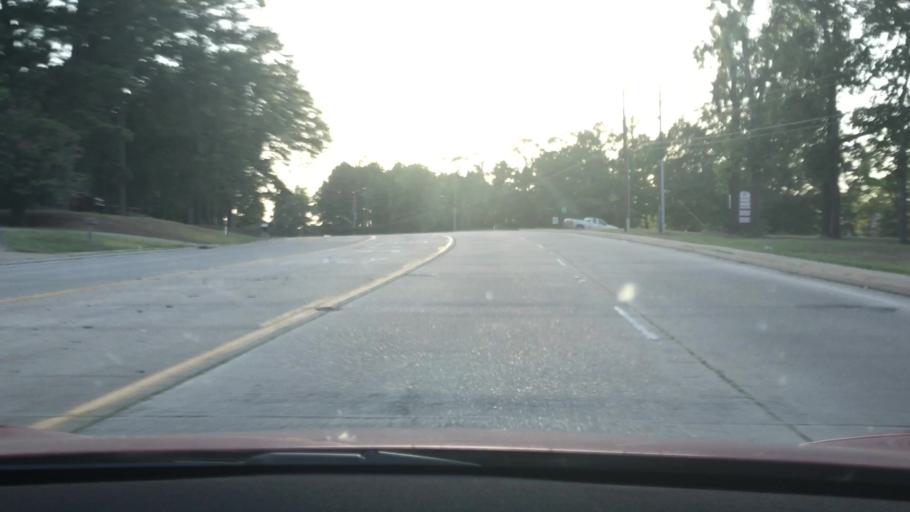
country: US
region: Louisiana
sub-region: Bossier Parish
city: Bossier City
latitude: 32.4018
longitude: -93.7840
